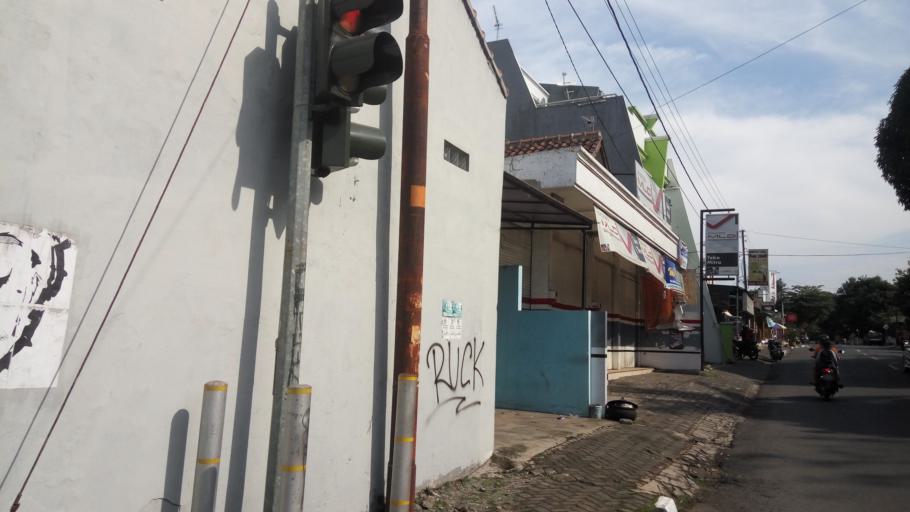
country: ID
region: Central Java
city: Ungaran
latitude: -7.1364
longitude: 110.4100
